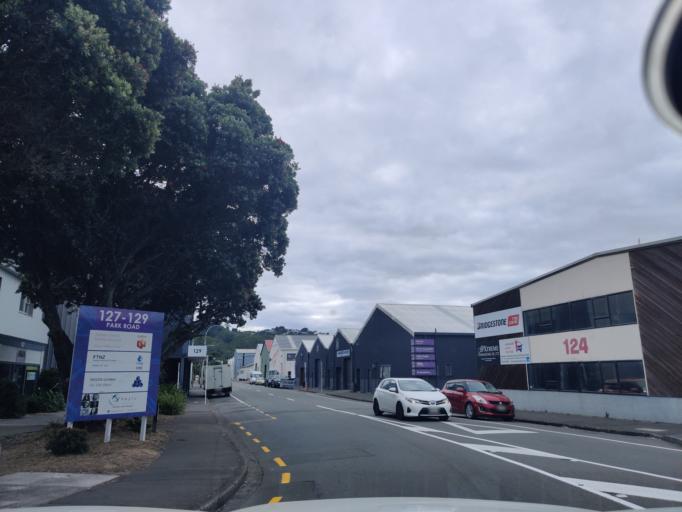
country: NZ
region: Wellington
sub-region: Wellington City
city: Wellington
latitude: -41.3102
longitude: 174.8209
